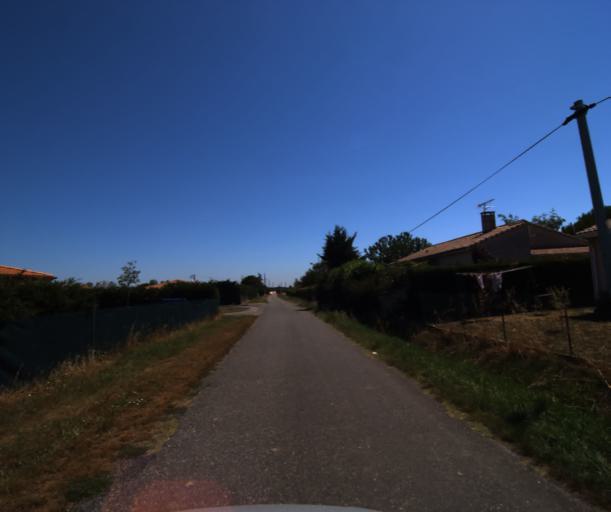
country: FR
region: Midi-Pyrenees
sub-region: Departement de la Haute-Garonne
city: Seysses
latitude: 43.4699
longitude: 1.3100
